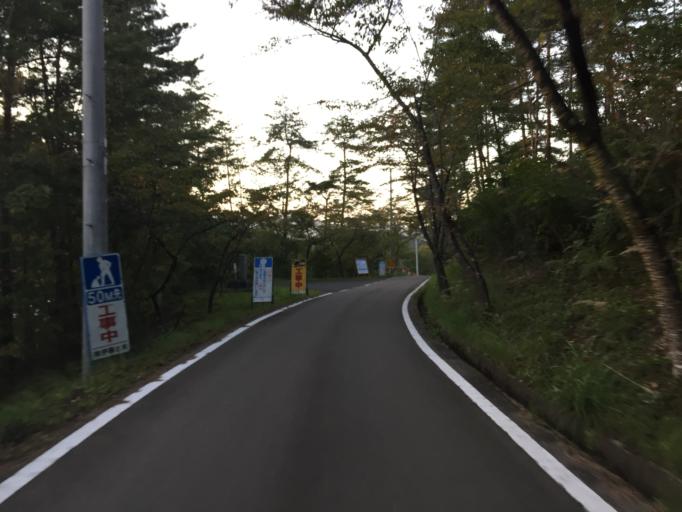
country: JP
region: Fukushima
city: Yanagawamachi-saiwaicho
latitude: 37.8499
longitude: 140.6315
